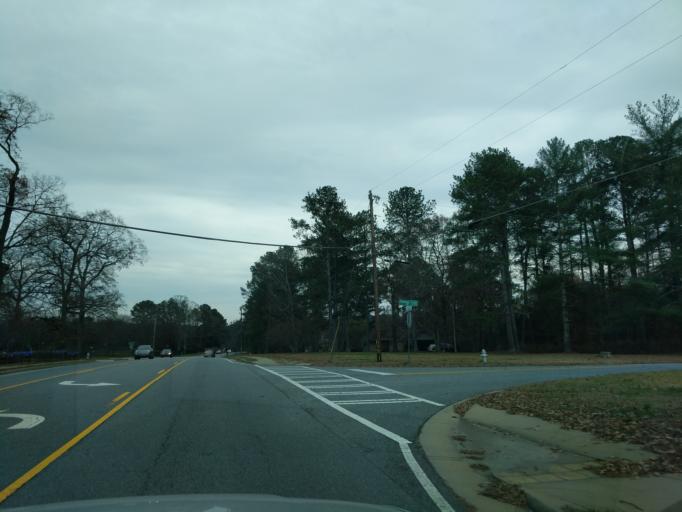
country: US
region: Georgia
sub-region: Gwinnett County
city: Duluth
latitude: 34.0181
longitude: -84.1566
